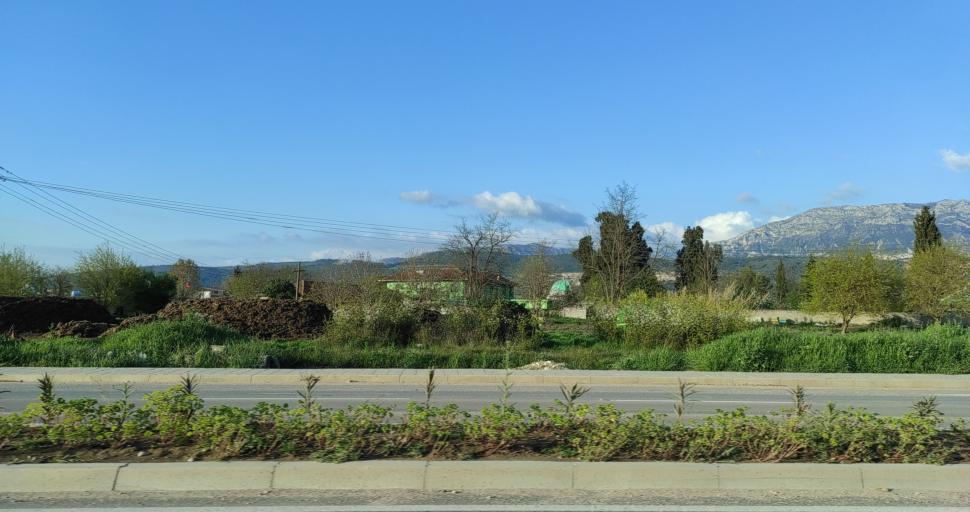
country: AL
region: Durres
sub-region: Rrethi i Krujes
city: Fushe-Kruje
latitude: 41.4862
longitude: 19.7279
